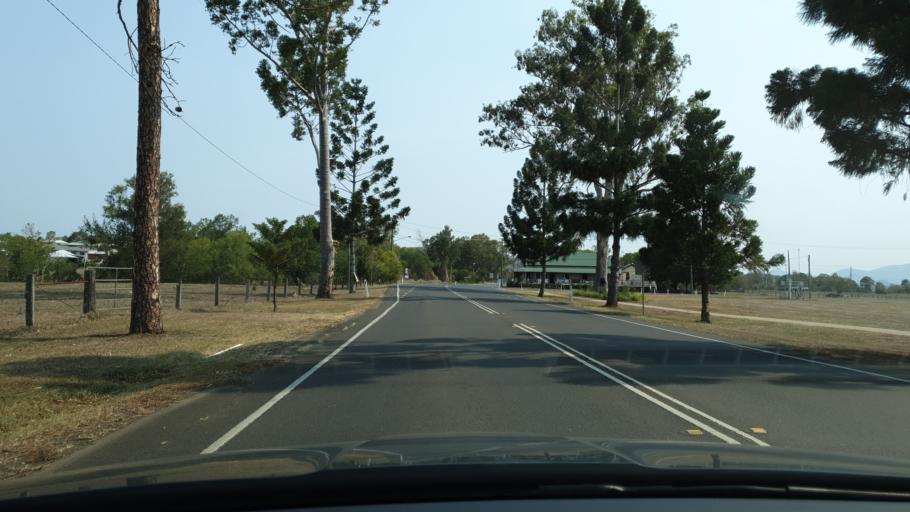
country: AU
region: Queensland
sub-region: Ipswich
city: Deebing Heights
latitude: -28.0031
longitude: 152.6813
